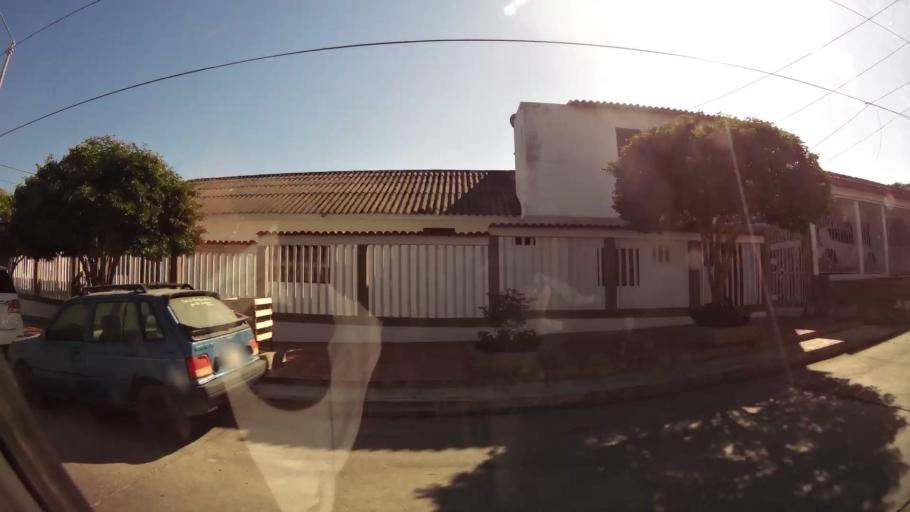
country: CO
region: Atlantico
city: Barranquilla
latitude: 10.9638
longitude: -74.7876
